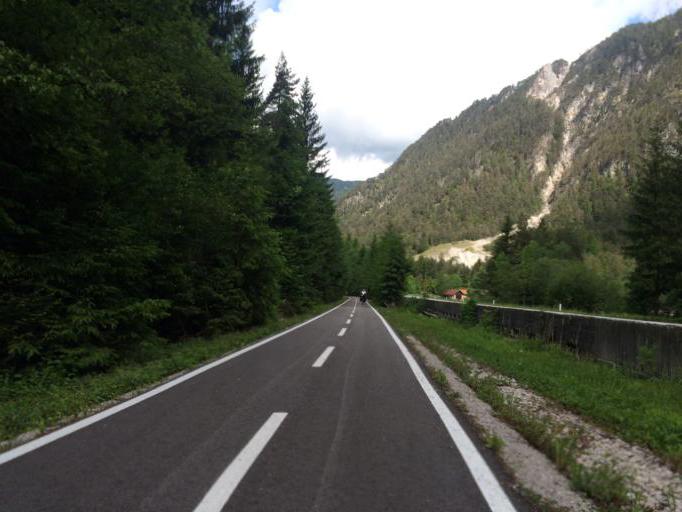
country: IT
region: Friuli Venezia Giulia
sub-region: Provincia di Udine
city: Malborghetto
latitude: 46.5063
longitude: 13.4926
